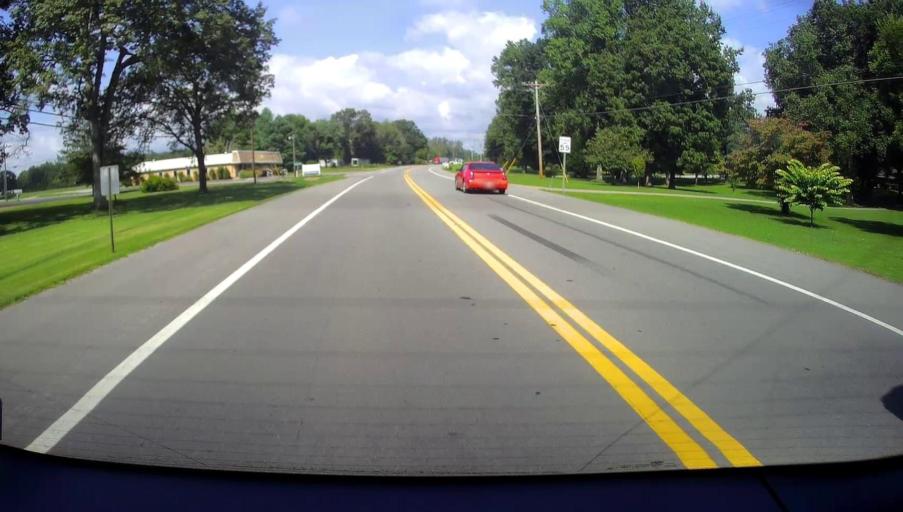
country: US
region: Tennessee
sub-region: Coffee County
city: Manchester
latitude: 35.4988
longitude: -86.1092
